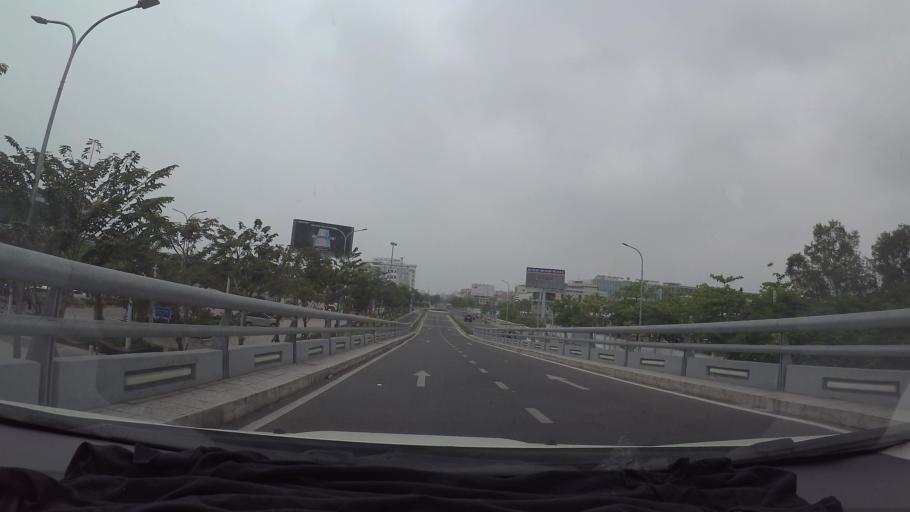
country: VN
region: Da Nang
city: Thanh Khe
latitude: 16.0565
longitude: 108.2039
